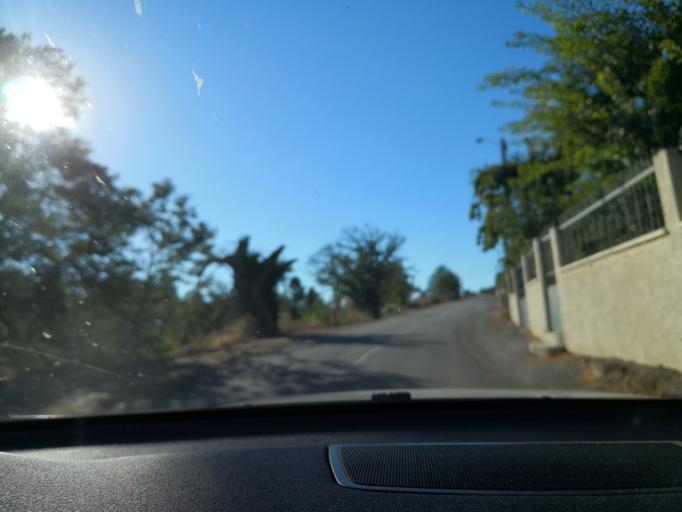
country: PT
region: Vila Real
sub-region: Sabrosa
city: Vilela
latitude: 41.2408
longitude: -7.6155
